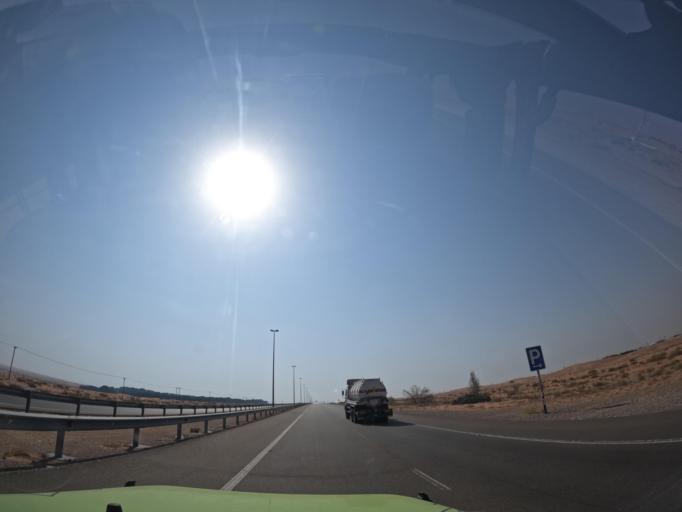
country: OM
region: Al Buraimi
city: Al Buraymi
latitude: 24.4199
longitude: 55.6905
